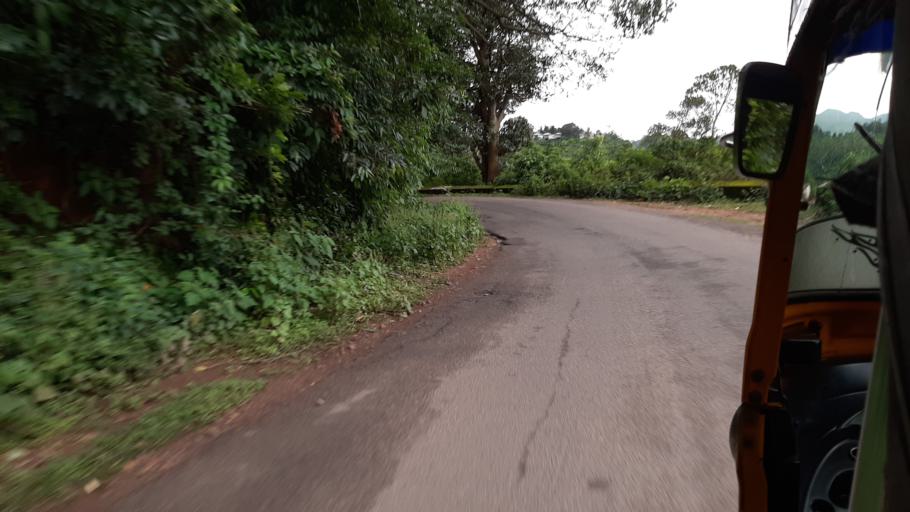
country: IN
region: Andhra Pradesh
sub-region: Vizianagaram District
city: Salur
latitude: 18.2425
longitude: 83.0175
